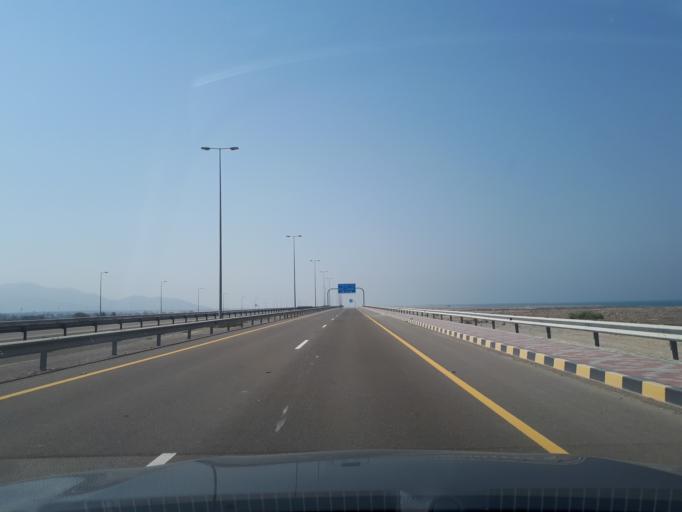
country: AE
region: Al Fujayrah
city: Al Fujayrah
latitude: 24.9421
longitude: 56.3817
